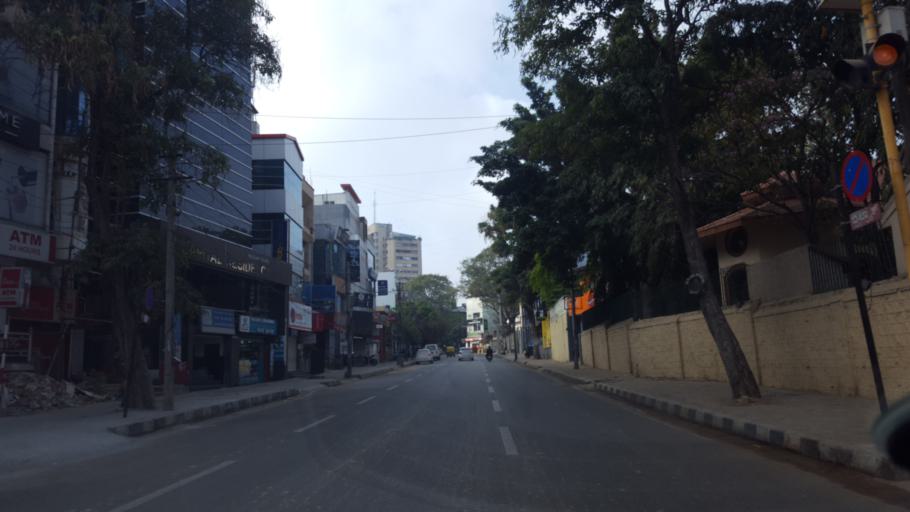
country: IN
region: Karnataka
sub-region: Bangalore Urban
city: Bangalore
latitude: 12.9701
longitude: 77.6066
